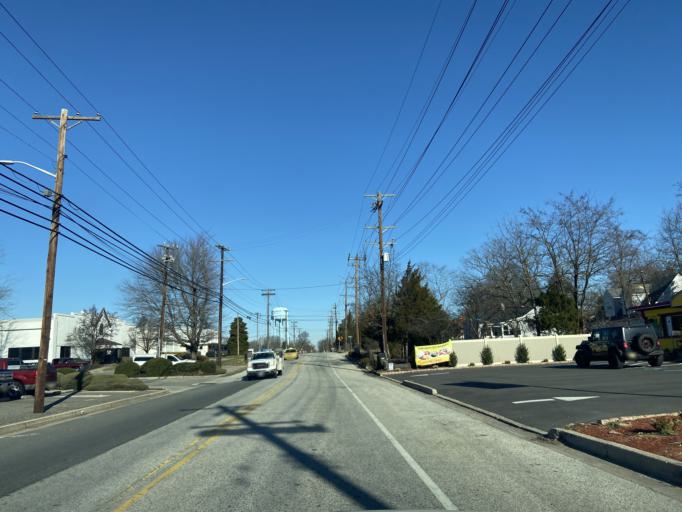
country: US
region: New Jersey
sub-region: Cumberland County
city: Vineland
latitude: 39.4921
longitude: -75.0611
